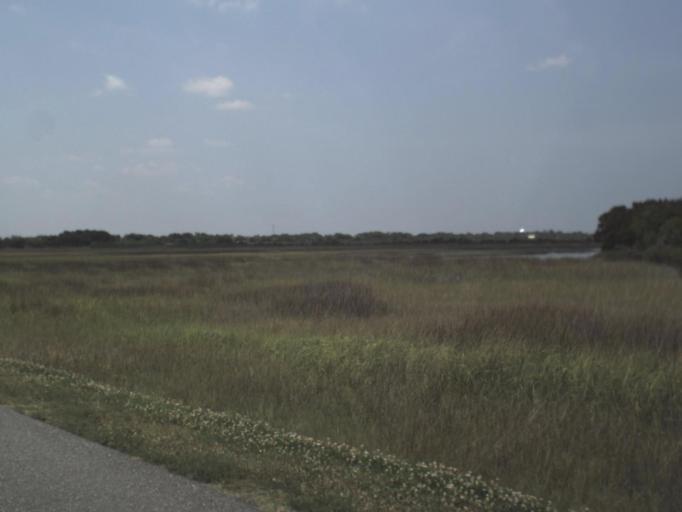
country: US
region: Florida
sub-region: Duval County
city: Atlantic Beach
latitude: 30.3765
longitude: -81.4365
